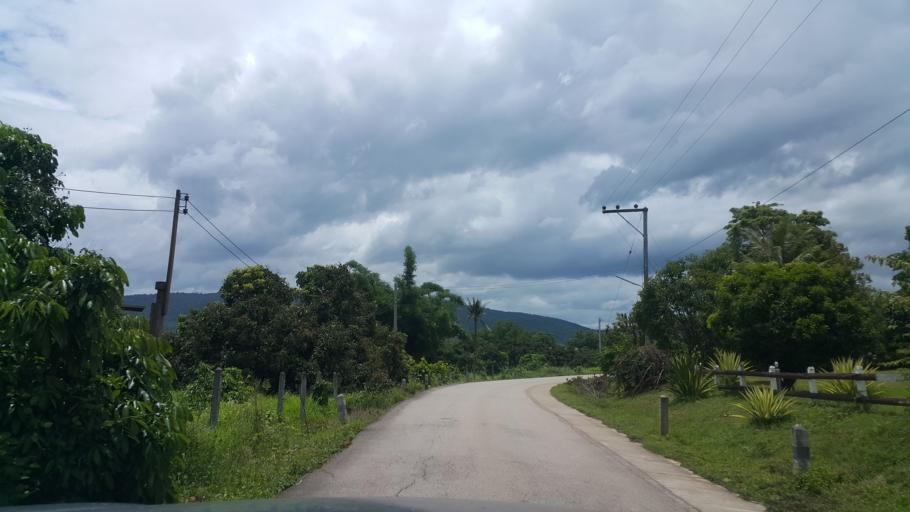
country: TH
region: Chiang Mai
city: Mae Taeng
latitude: 19.2065
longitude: 99.0057
